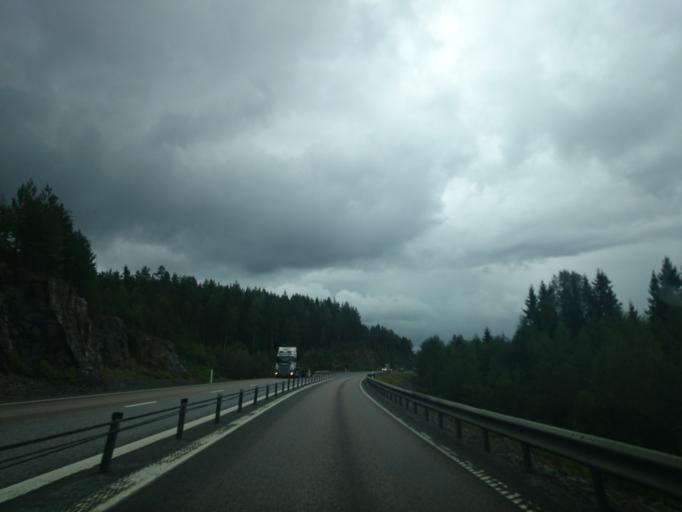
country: SE
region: Vaesternorrland
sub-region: Kramfors Kommun
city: Nordingra
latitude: 62.9433
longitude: 18.0940
